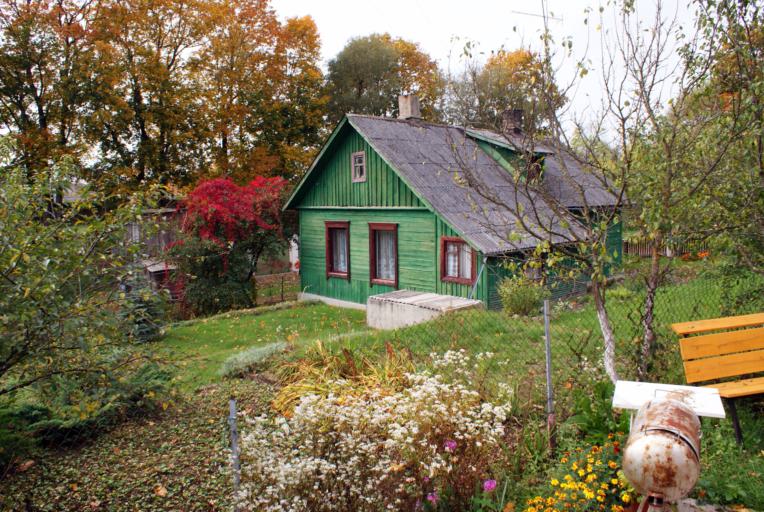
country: LV
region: Dagda
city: Dagda
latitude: 56.0926
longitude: 27.5391
